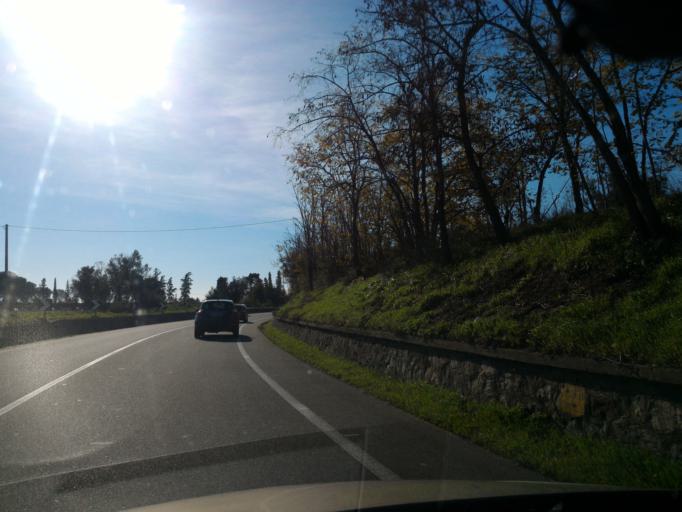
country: IT
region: Calabria
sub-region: Provincia di Crotone
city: Tronca
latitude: 39.2111
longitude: 17.1095
